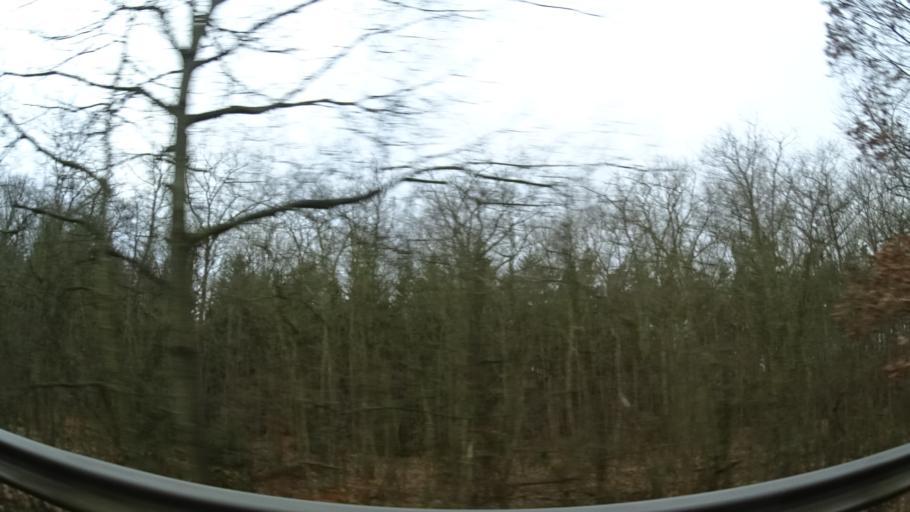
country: DE
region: Rheinland-Pfalz
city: Daubach
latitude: 49.8354
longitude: 7.6351
